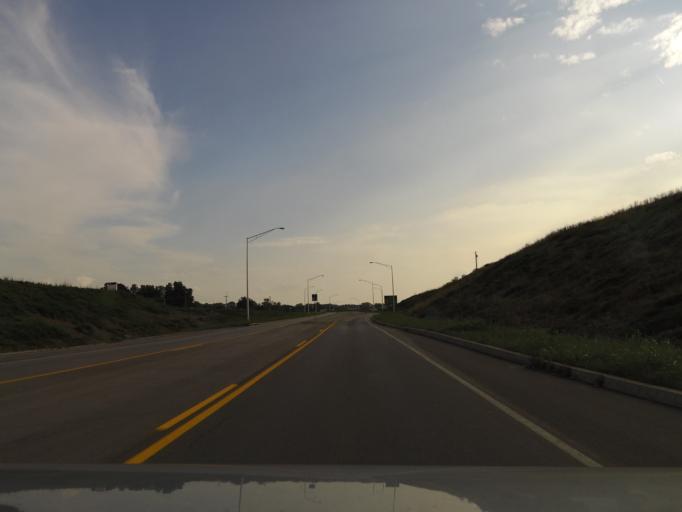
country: US
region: Kentucky
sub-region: Harrison County
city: Cynthiana
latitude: 38.3705
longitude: -84.3182
